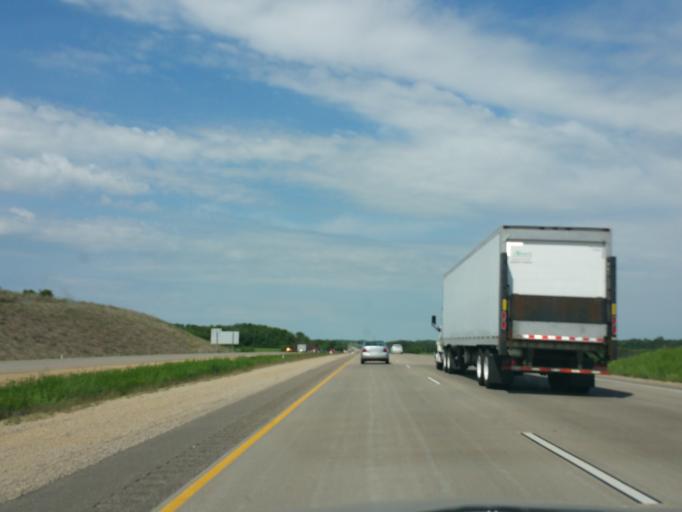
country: US
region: Wisconsin
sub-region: Saint Croix County
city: Roberts
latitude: 44.9606
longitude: -92.5671
